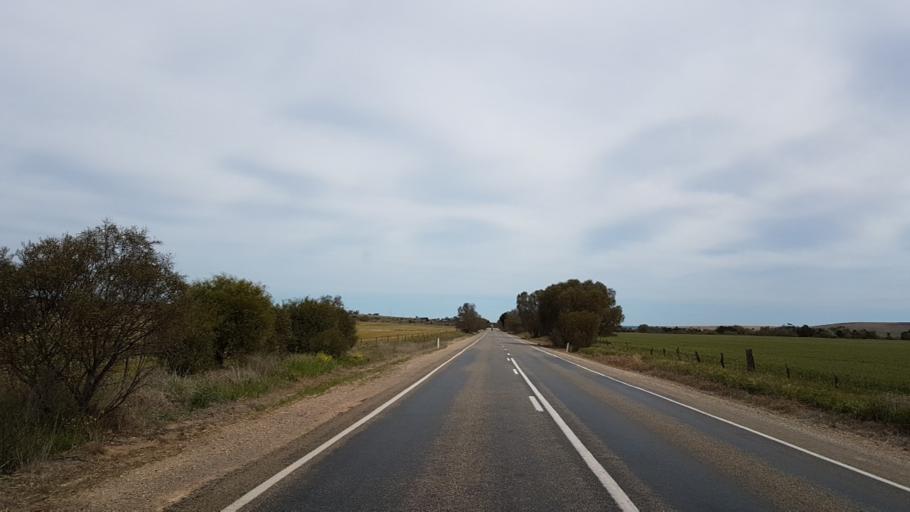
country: AU
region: South Australia
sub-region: Northern Areas
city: Jamestown
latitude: -33.2172
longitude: 138.4156
